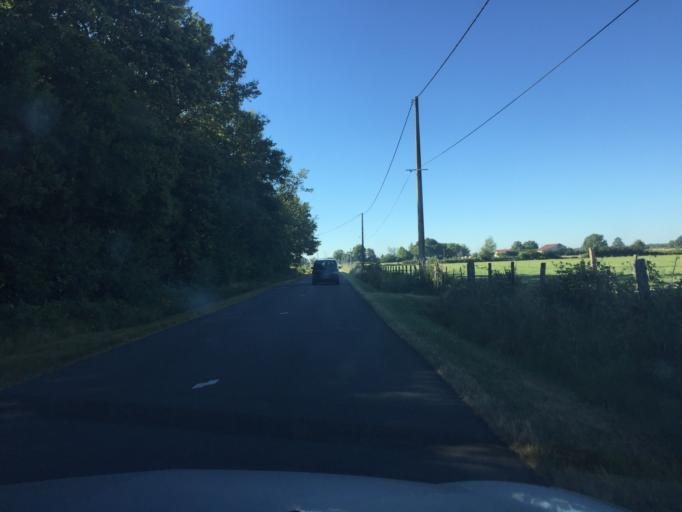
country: FR
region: Auvergne
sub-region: Departement de l'Allier
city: Dompierre-sur-Besbre
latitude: 46.5240
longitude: 3.6204
